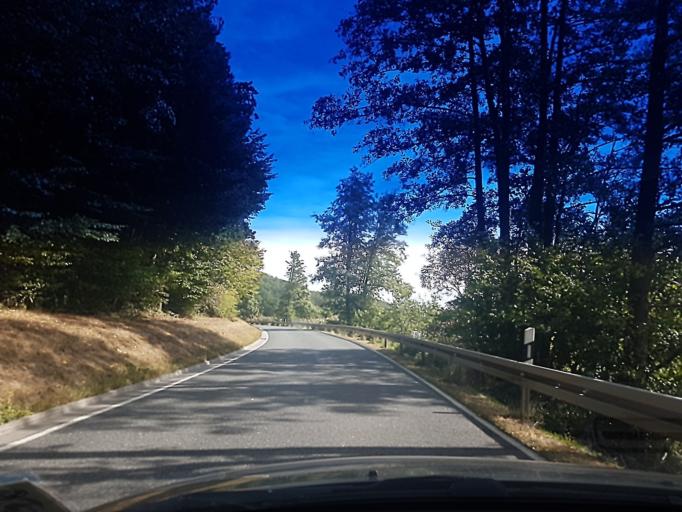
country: DE
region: Bavaria
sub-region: Regierungsbezirk Mittelfranken
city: Wachenroth
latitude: 49.7730
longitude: 10.7144
